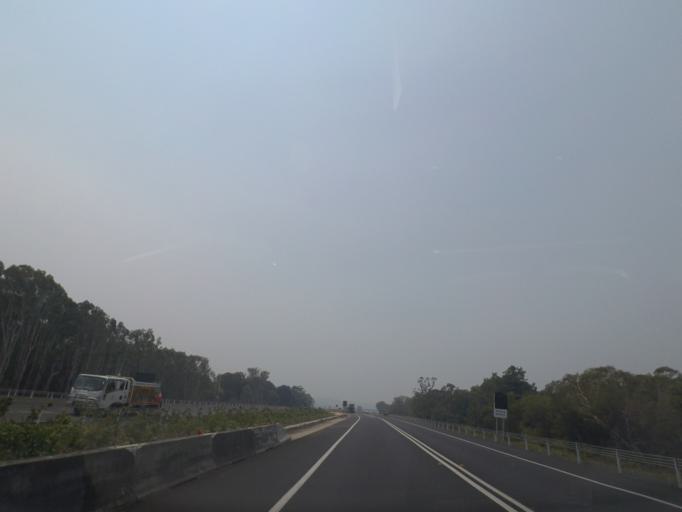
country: AU
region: New South Wales
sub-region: Ballina
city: Ballina
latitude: -28.9111
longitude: 153.4788
